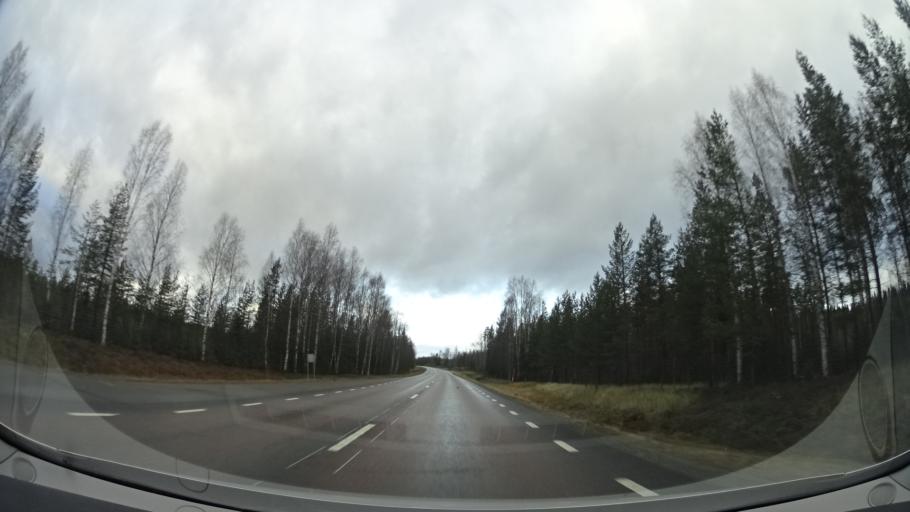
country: SE
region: Vaesterbotten
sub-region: Skelleftea Kommun
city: Viken
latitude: 64.7977
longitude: 20.7391
